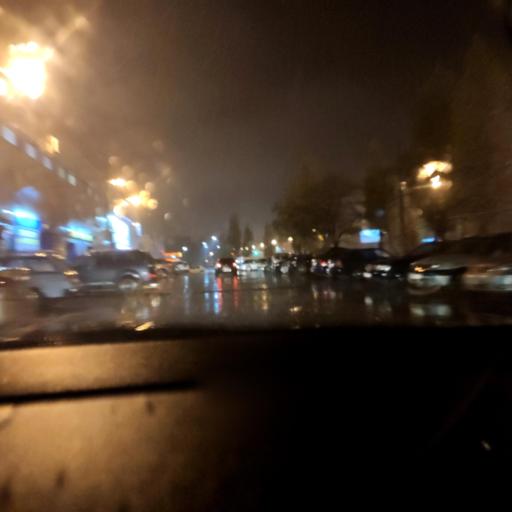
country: RU
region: Voronezj
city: Voronezh
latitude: 51.6454
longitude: 39.1325
